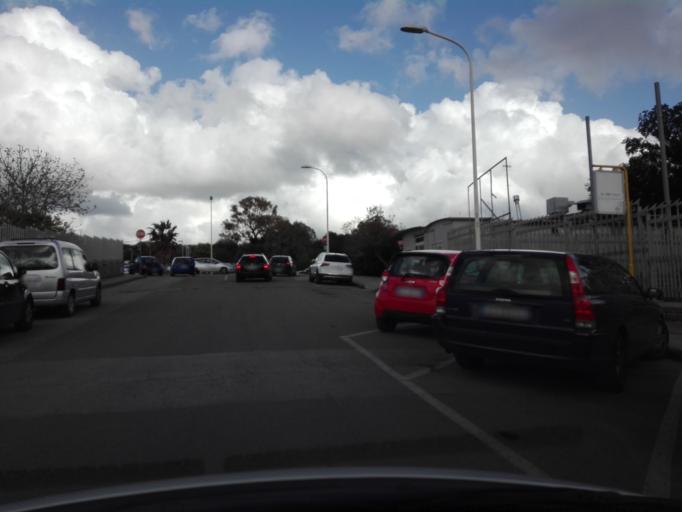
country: IT
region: Sardinia
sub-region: Provincia di Sassari
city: Sassari
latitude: 40.7191
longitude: 8.5813
